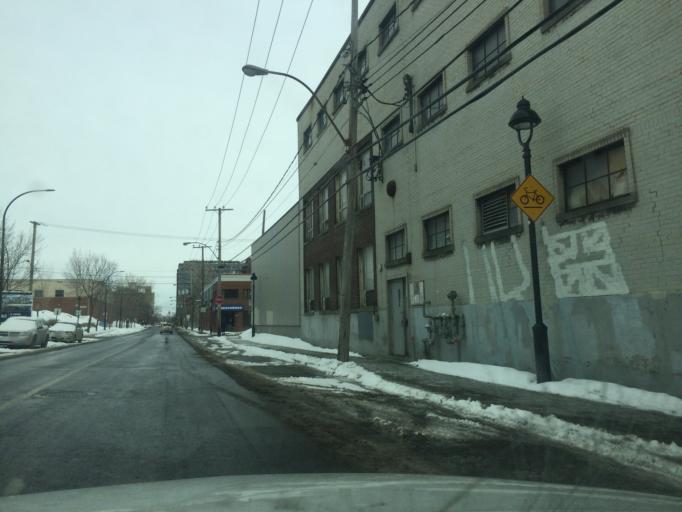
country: CA
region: Quebec
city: Westmount
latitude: 45.4827
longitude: -73.5674
